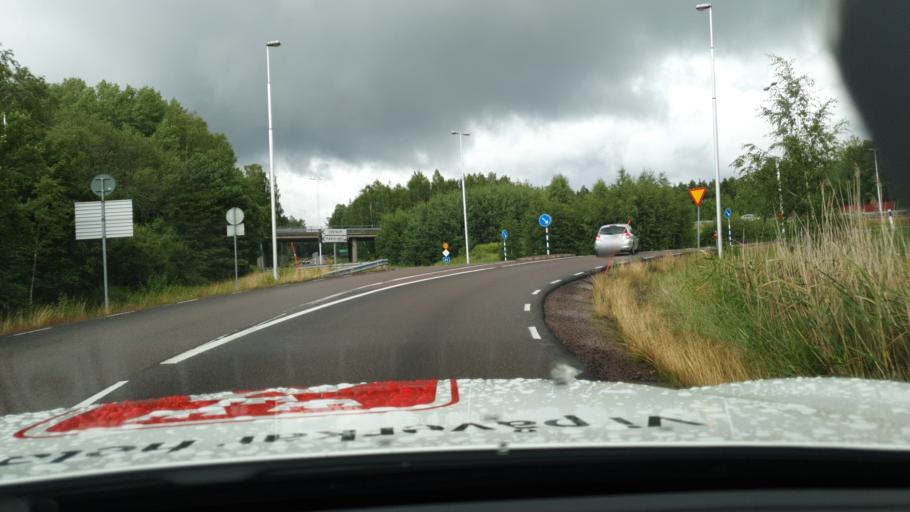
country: SE
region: Vaermland
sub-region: Kristinehamns Kommun
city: Kristinehamn
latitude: 59.3235
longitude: 14.1145
